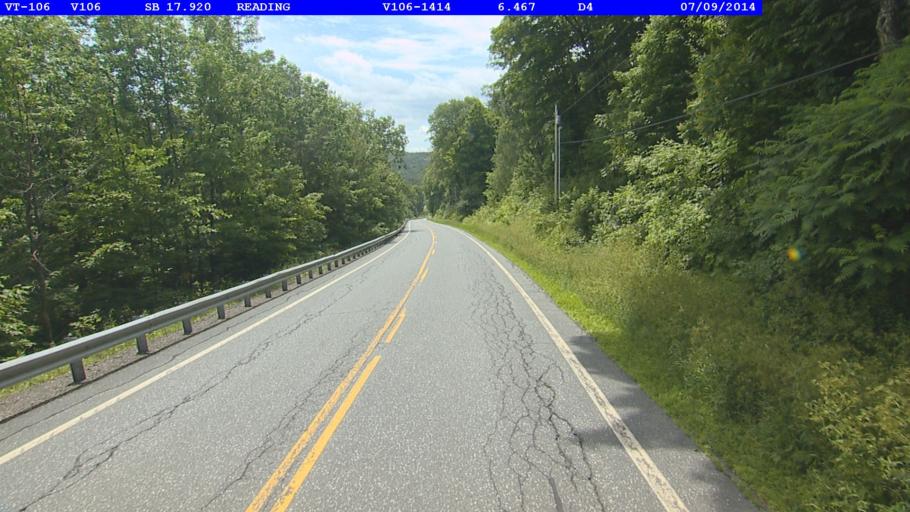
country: US
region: Vermont
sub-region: Windsor County
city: Woodstock
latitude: 43.5274
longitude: -72.5547
